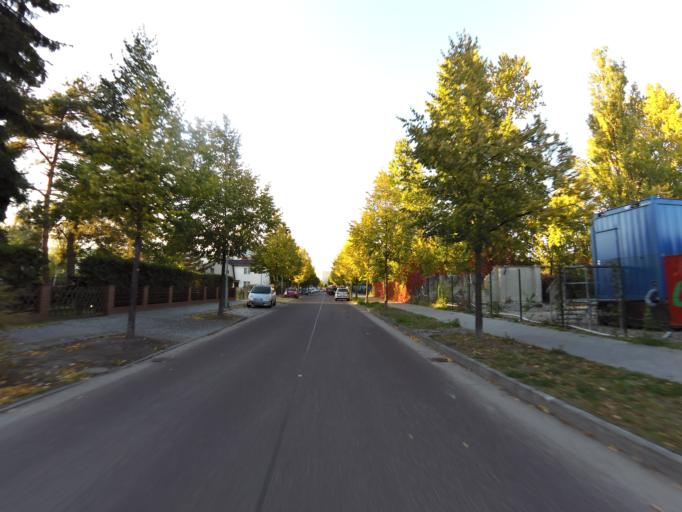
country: DE
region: Berlin
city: Johannisthal
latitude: 52.4357
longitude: 13.5079
